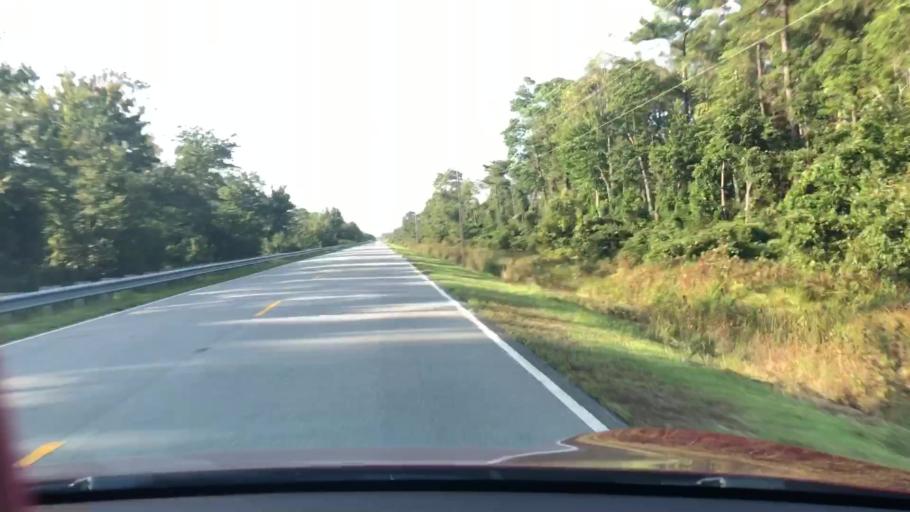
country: US
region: North Carolina
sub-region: Dare County
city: Wanchese
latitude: 35.7390
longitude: -75.7686
